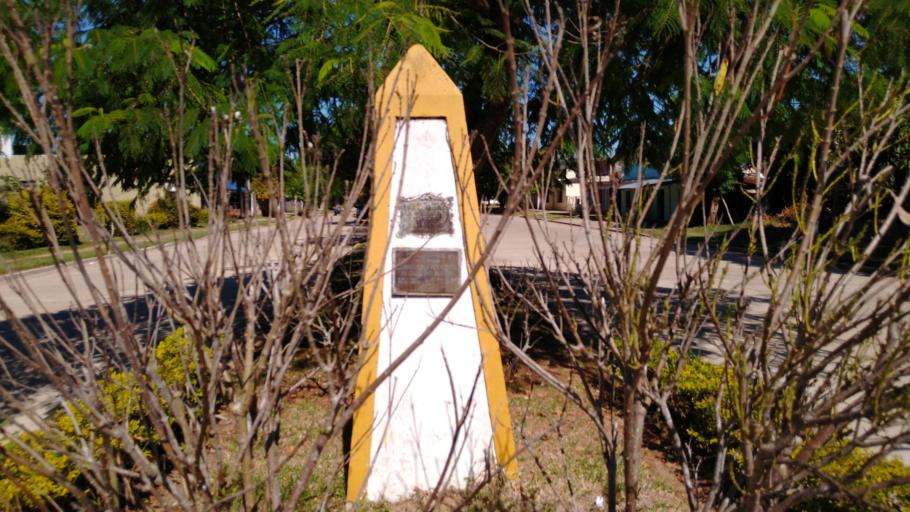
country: AR
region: Corrientes
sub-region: Departamento de San Miguel
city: San Miguel
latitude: -27.9957
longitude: -57.5926
